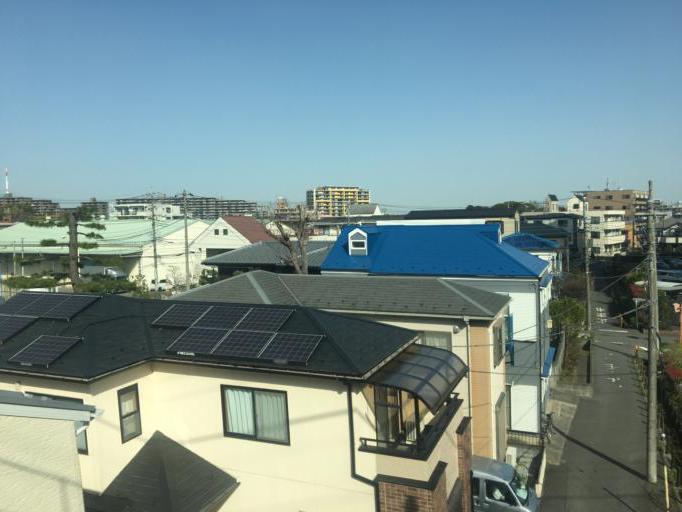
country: JP
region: Saitama
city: Yono
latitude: 35.8476
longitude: 139.6330
